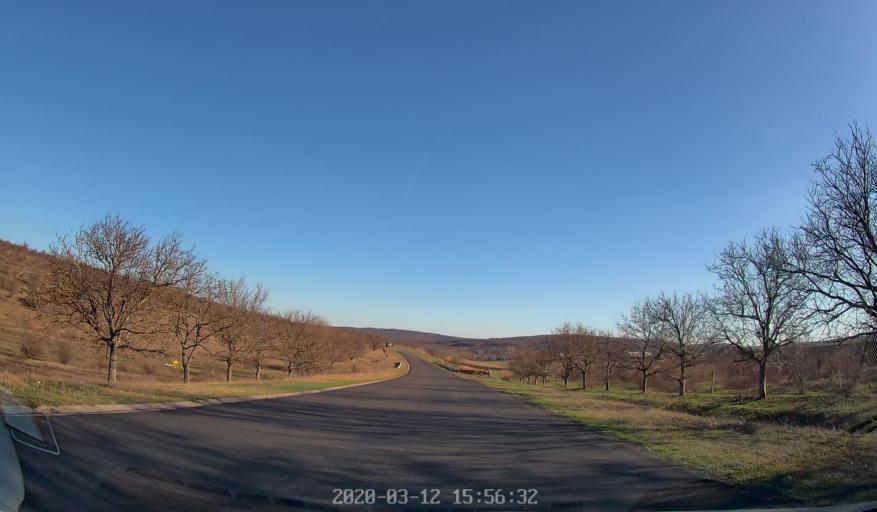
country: MD
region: Chisinau
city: Vadul lui Voda
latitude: 47.0621
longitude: 29.0336
